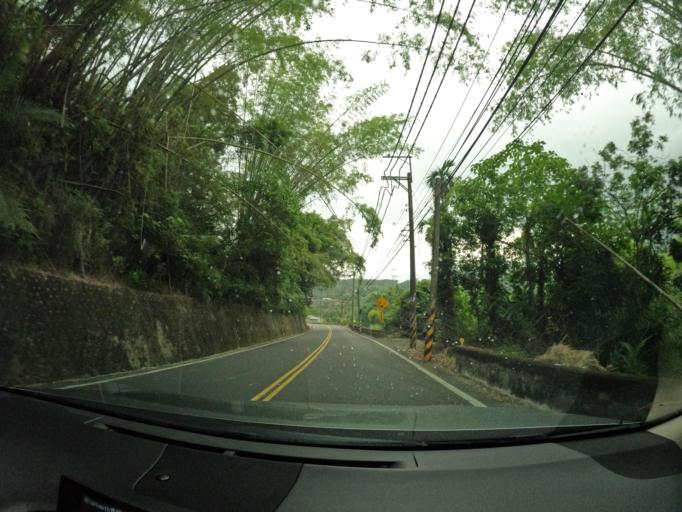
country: TW
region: Taiwan
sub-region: Nantou
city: Nantou
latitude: 23.8706
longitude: 120.7736
